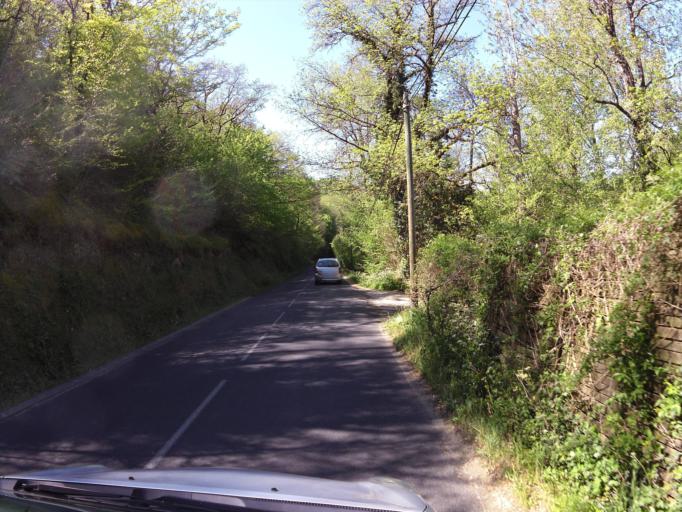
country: FR
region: Aquitaine
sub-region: Departement de la Dordogne
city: Cenac-et-Saint-Julien
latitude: 44.8014
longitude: 1.1600
